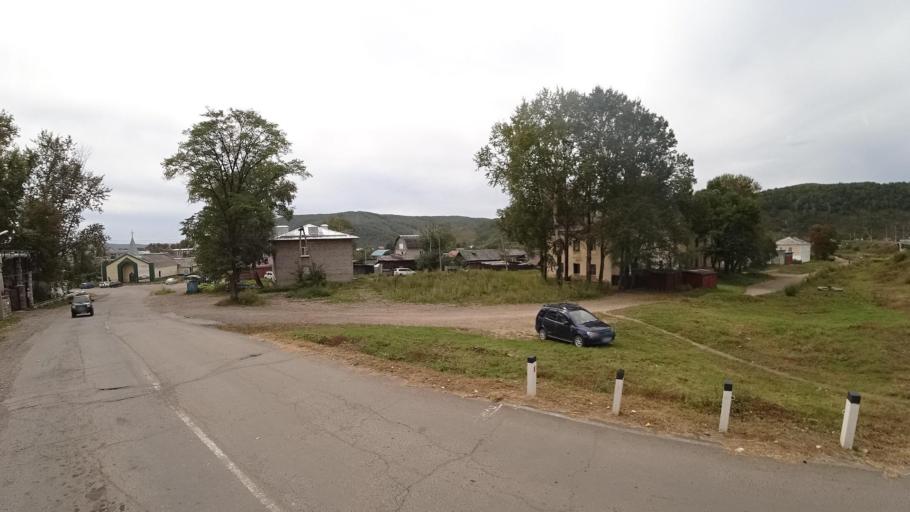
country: RU
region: Jewish Autonomous Oblast
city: Khingansk
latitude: 49.0168
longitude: 131.0547
